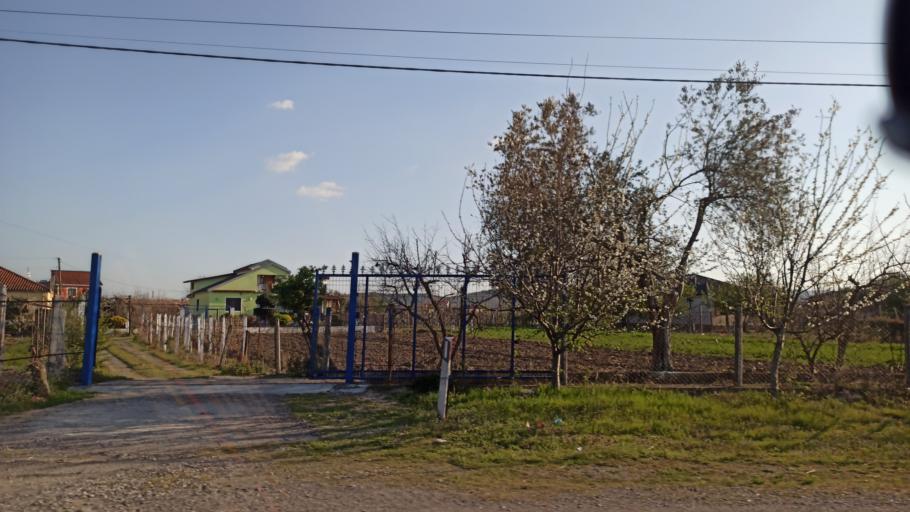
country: AL
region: Shkoder
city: Vukatane
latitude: 41.9907
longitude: 19.5750
